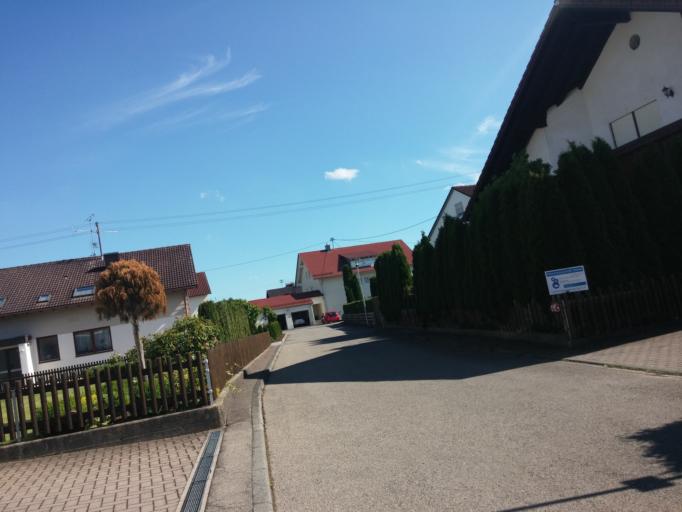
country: DE
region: Baden-Wuerttemberg
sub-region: Tuebingen Region
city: Berkheim
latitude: 48.0412
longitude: 10.0876
